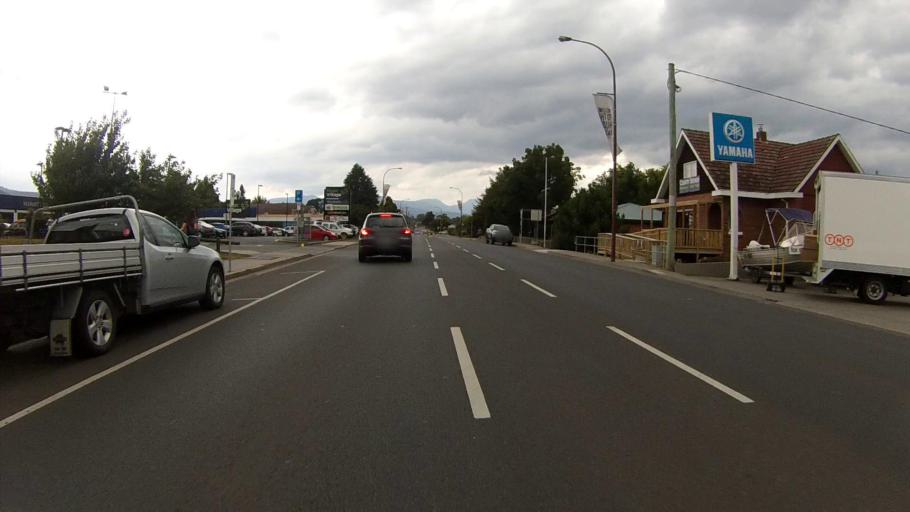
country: AU
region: Tasmania
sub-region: Huon Valley
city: Huonville
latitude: -43.0289
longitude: 147.0495
